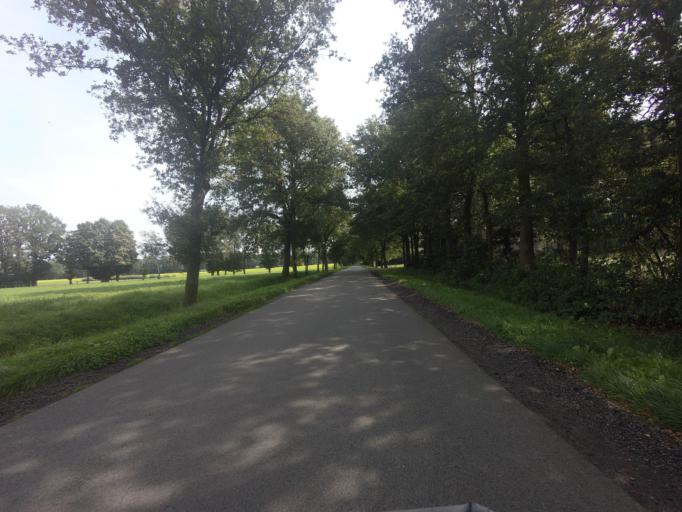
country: DE
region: Lower Saxony
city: Itterbeck
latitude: 52.5264
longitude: 6.7705
